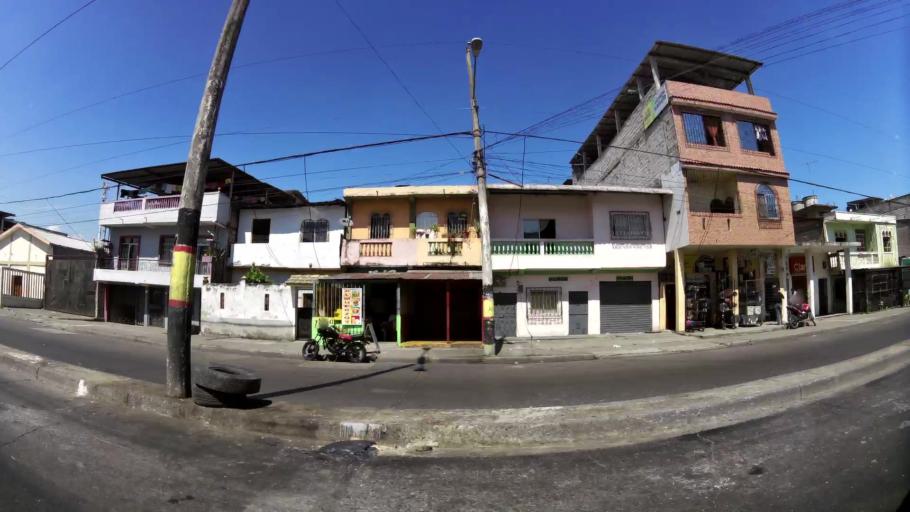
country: EC
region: Guayas
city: Guayaquil
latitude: -2.2248
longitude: -79.9428
